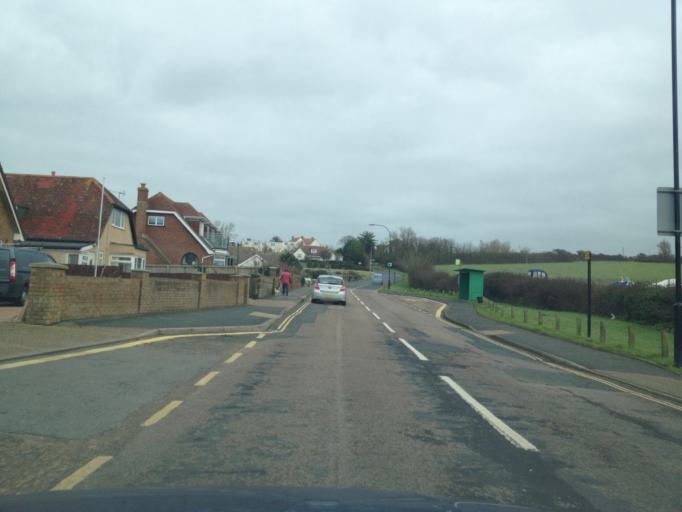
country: GB
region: England
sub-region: Isle of Wight
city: Brading
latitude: 50.6624
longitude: -1.1356
